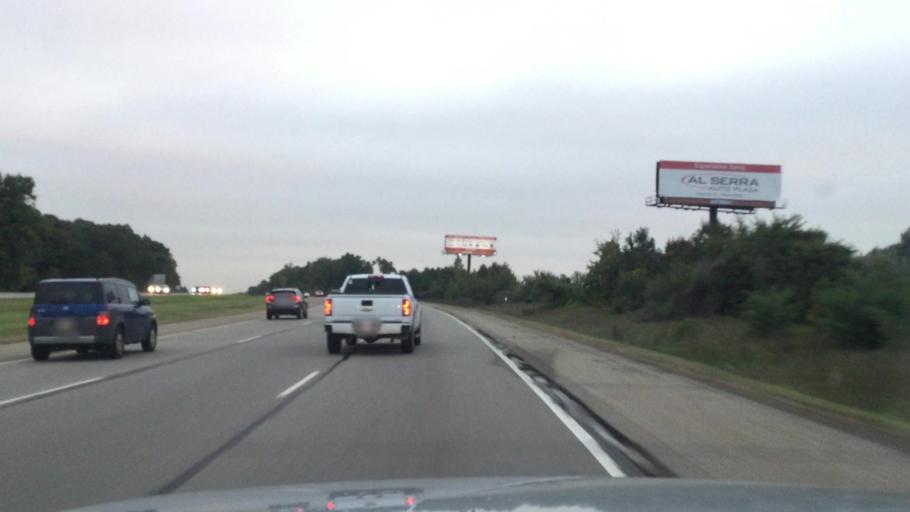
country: US
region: Michigan
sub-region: Oakland County
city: Holly
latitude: 42.8211
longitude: -83.5700
